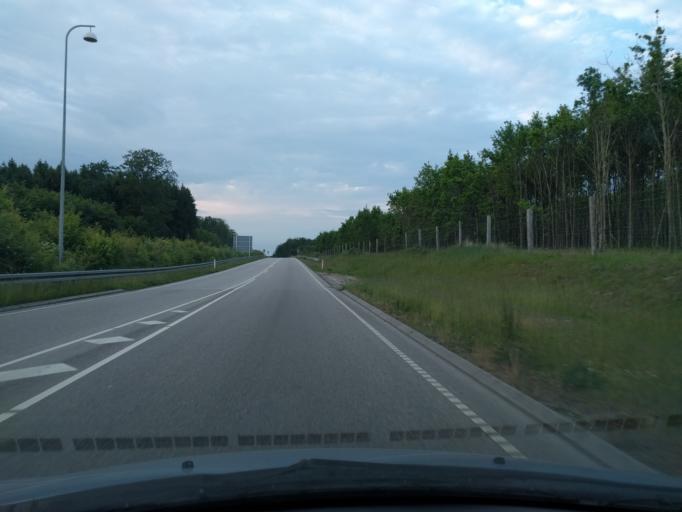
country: DK
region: Zealand
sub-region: Naestved Kommune
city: Naestved
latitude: 55.2323
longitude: 11.7983
